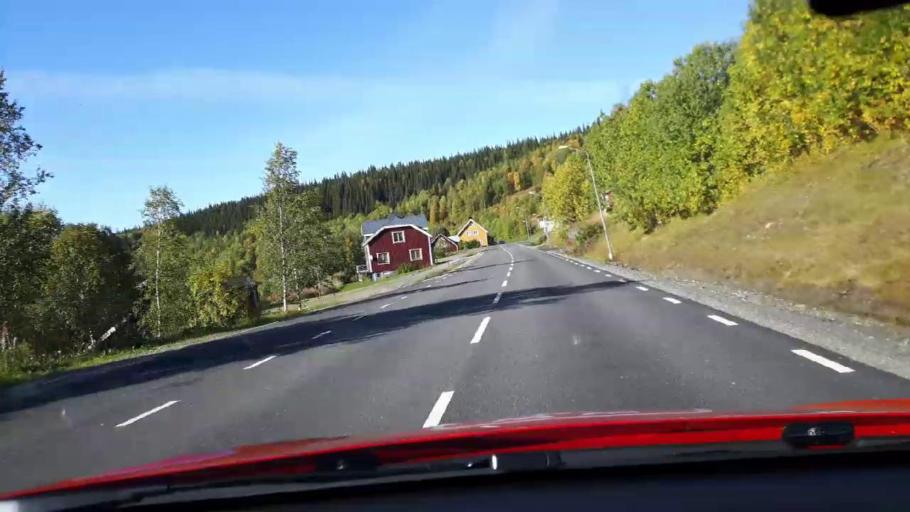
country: NO
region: Nord-Trondelag
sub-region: Royrvik
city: Royrvik
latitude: 64.8349
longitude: 14.1088
